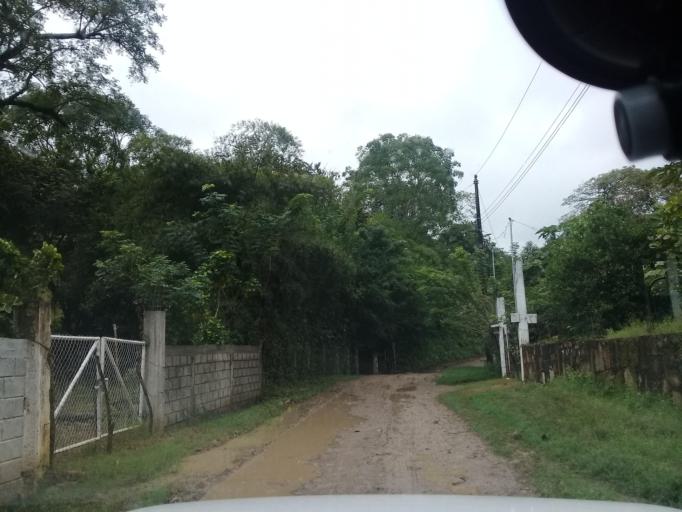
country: MX
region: Veracruz
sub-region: Chalma
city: San Pedro Coyutla
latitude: 21.2382
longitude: -98.4252
